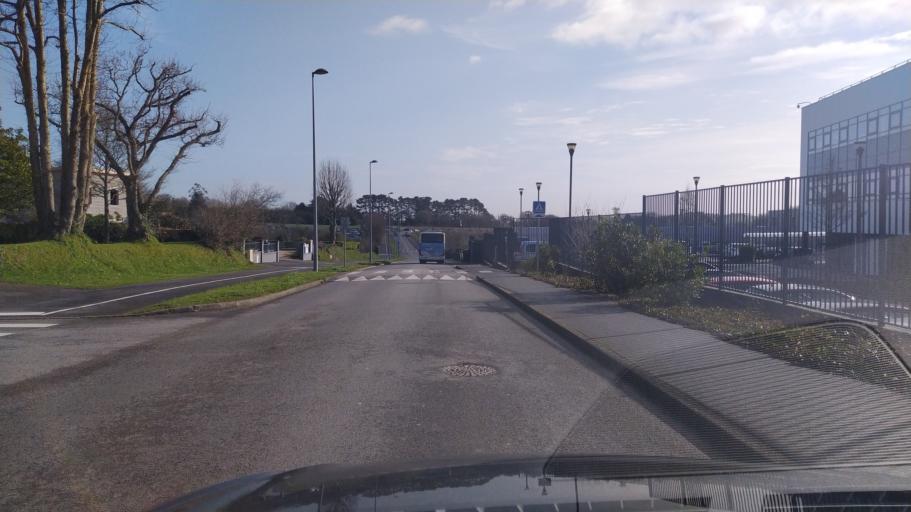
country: FR
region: Brittany
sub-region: Departement du Finistere
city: Gouesnou
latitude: 48.4198
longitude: -4.4514
